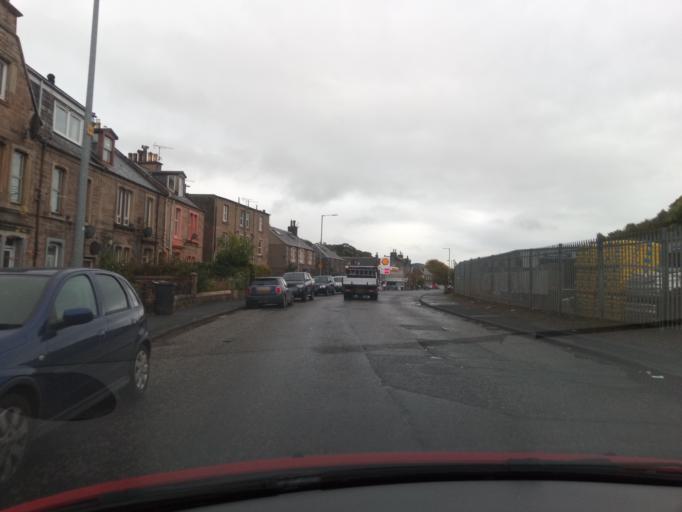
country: GB
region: Scotland
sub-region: The Scottish Borders
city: Galashiels
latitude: 55.6218
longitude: -2.8187
